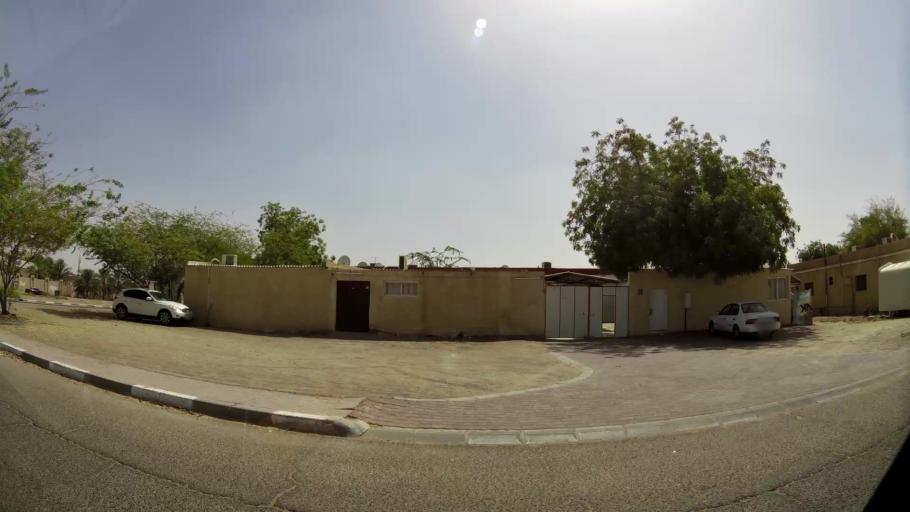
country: AE
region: Abu Dhabi
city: Al Ain
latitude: 24.2249
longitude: 55.6932
